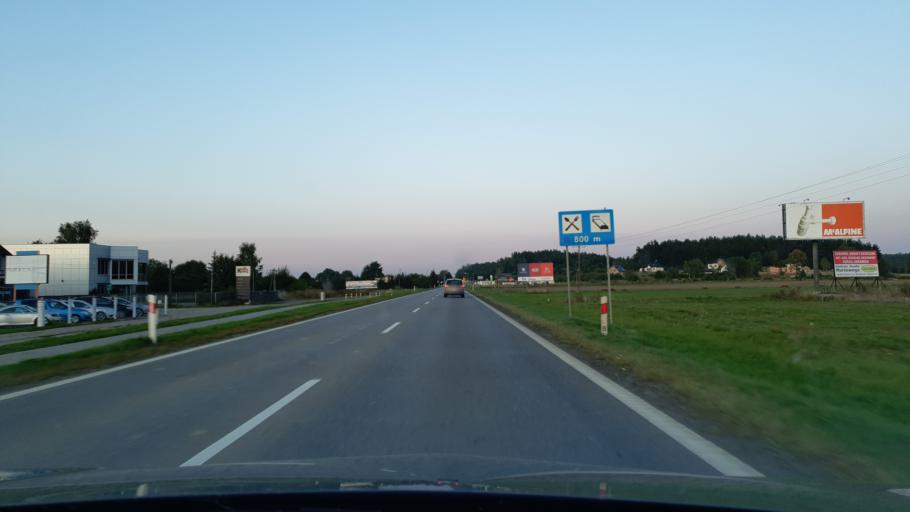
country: PL
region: Pomeranian Voivodeship
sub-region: Powiat leborski
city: Lebork
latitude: 54.5553
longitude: 17.8083
